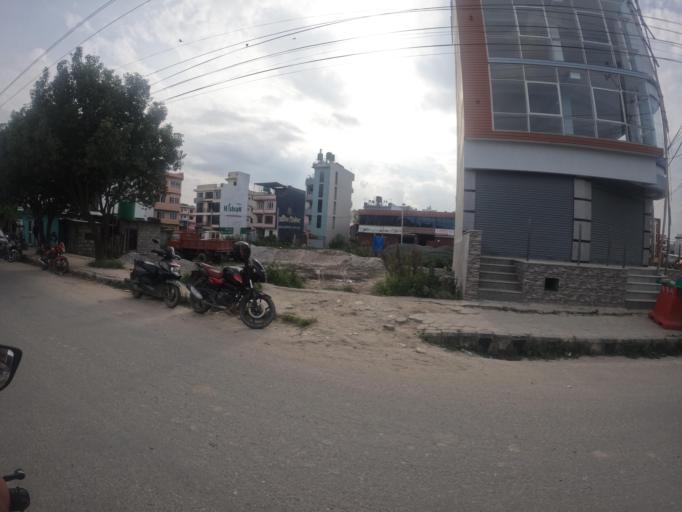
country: NP
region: Central Region
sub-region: Bagmati Zone
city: Bhaktapur
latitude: 27.6784
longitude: 85.3986
